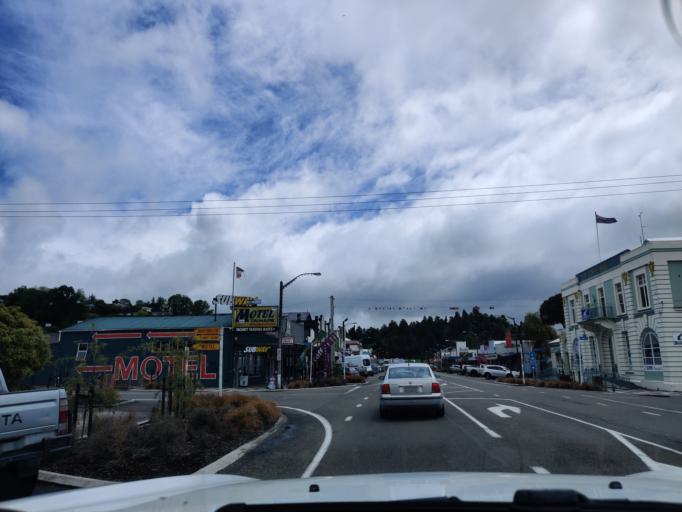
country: NZ
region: Manawatu-Wanganui
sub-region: Ruapehu District
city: Waiouru
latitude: -39.6791
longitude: 175.7998
